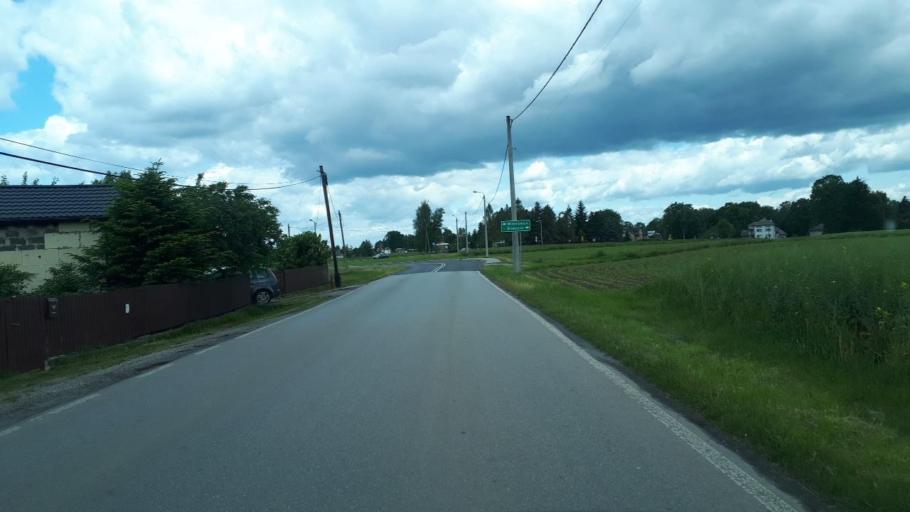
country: PL
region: Lesser Poland Voivodeship
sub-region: Powiat oswiecimski
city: Brzeszcze
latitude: 49.9550
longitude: 19.1385
